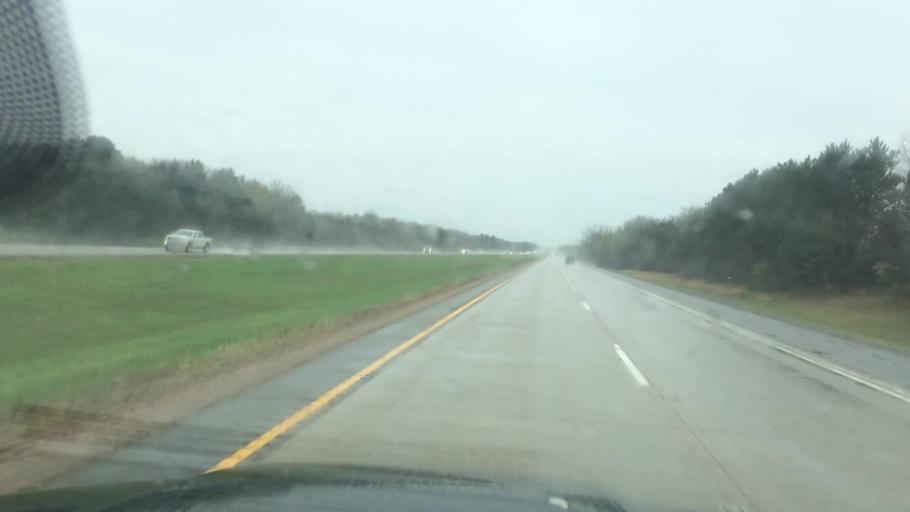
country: US
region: Wisconsin
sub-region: Portage County
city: Stevens Point
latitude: 44.6212
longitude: -89.6290
